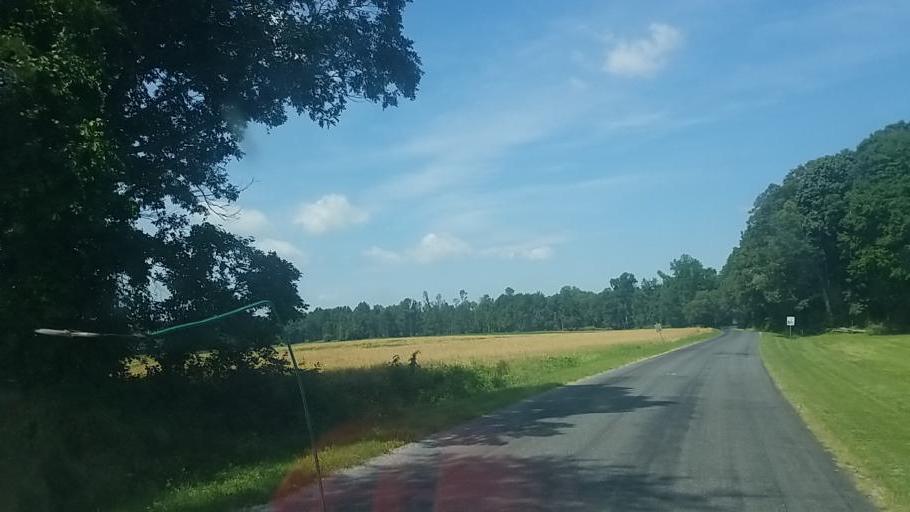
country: US
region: Maryland
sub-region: Caroline County
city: Denton
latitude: 38.8792
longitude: -75.7780
